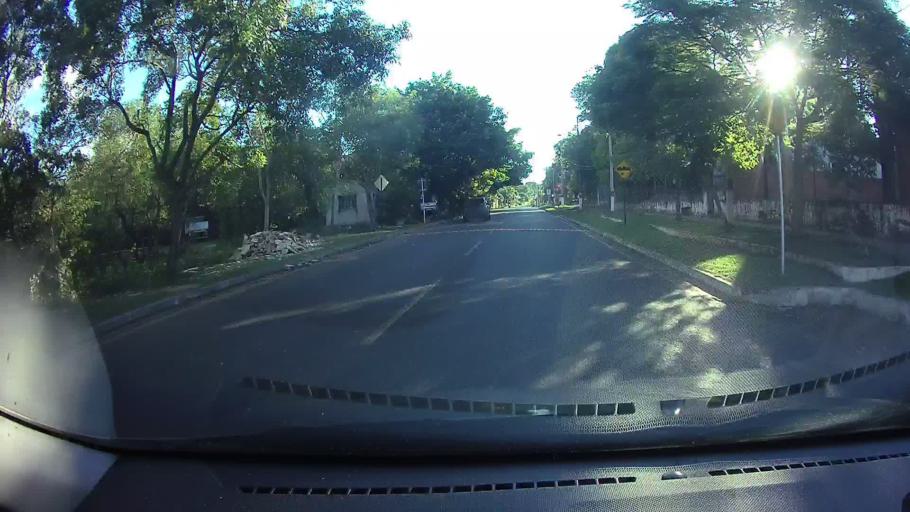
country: PY
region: Cordillera
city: Emboscada
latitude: -25.1891
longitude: -57.3062
